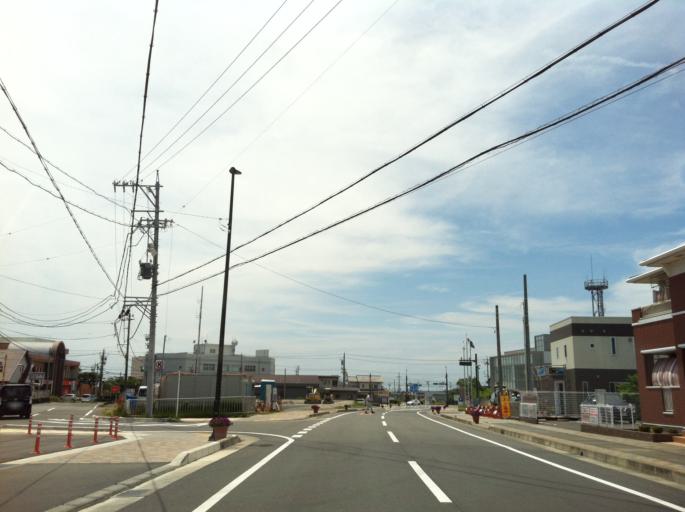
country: JP
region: Shizuoka
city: Sagara
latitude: 34.6404
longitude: 138.1274
